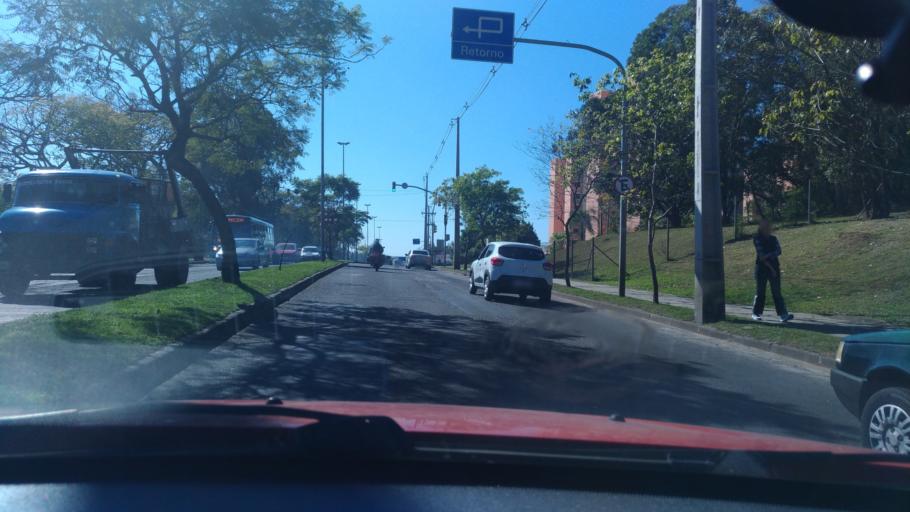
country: BR
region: Rio Grande do Sul
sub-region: Porto Alegre
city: Porto Alegre
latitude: -30.0435
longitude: -51.1393
